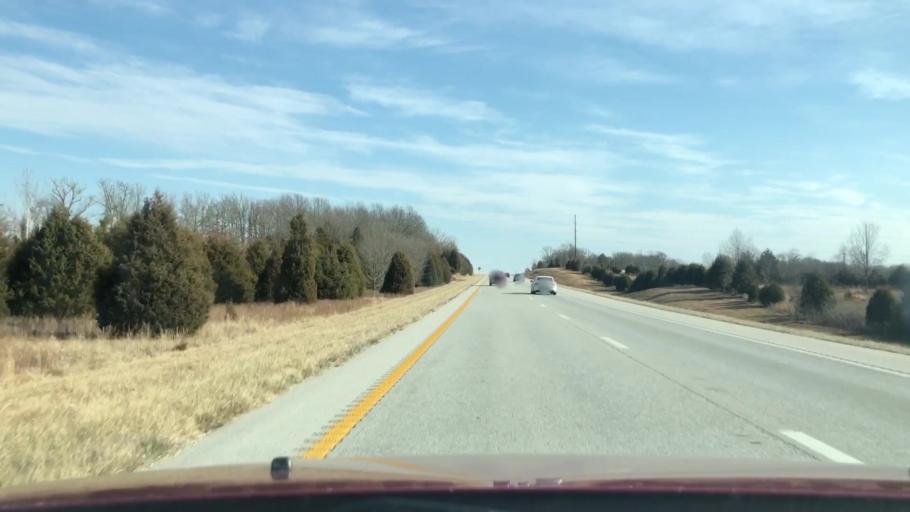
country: US
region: Missouri
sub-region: Webster County
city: Rogersville
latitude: 37.1201
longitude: -93.0081
